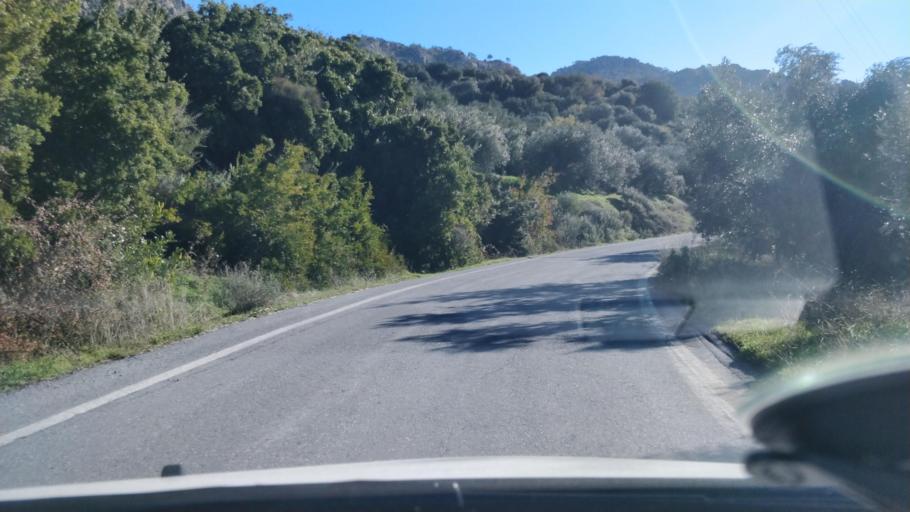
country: GR
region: Crete
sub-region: Nomos Lasithiou
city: Kritsa
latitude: 35.0794
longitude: 25.5961
